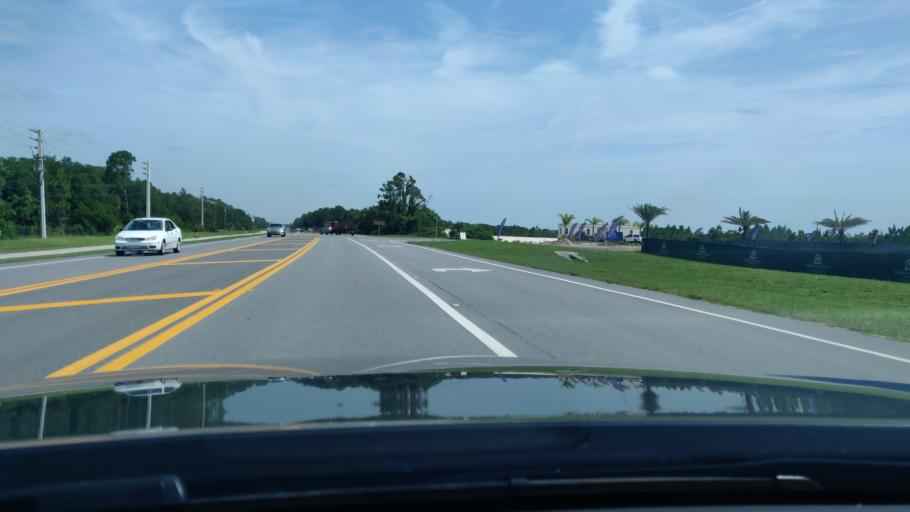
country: US
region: Florida
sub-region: Flagler County
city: Flagler Beach
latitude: 29.4996
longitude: -81.1579
